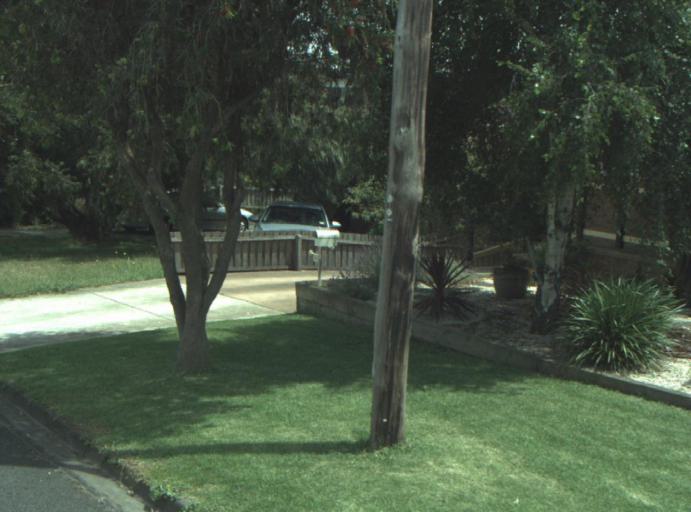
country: AU
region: Victoria
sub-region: Greater Geelong
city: Clifton Springs
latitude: -38.1605
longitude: 144.5582
